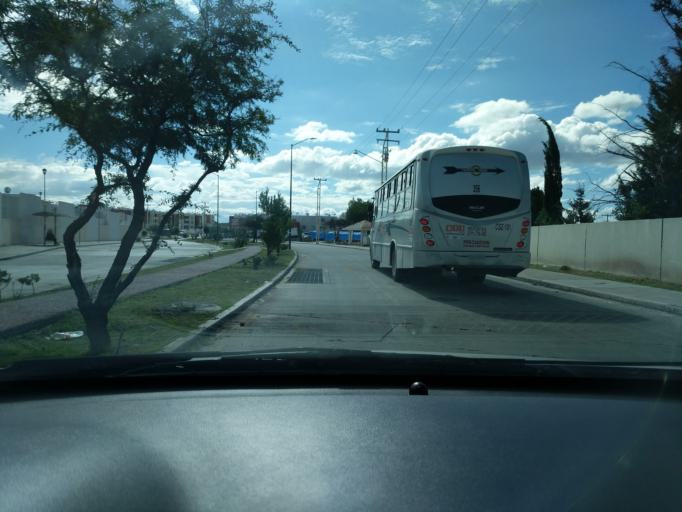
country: MX
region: Queretaro
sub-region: El Marques
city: La Loma
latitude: 20.5881
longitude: -100.2596
